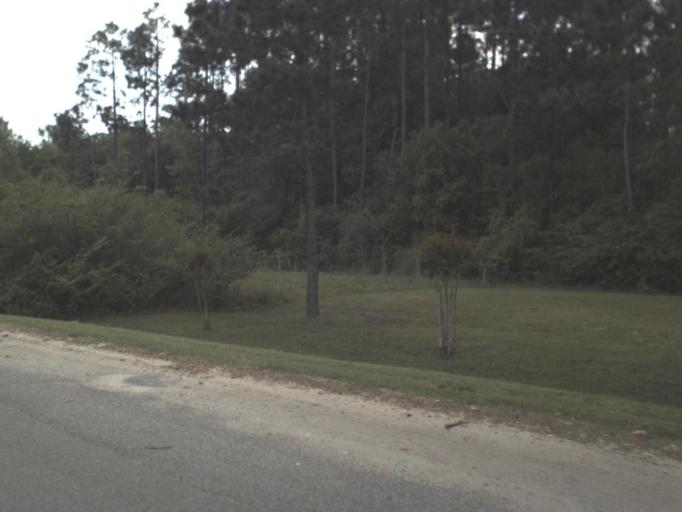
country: US
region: Florida
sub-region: Escambia County
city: Cantonment
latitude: 30.6053
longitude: -87.3165
